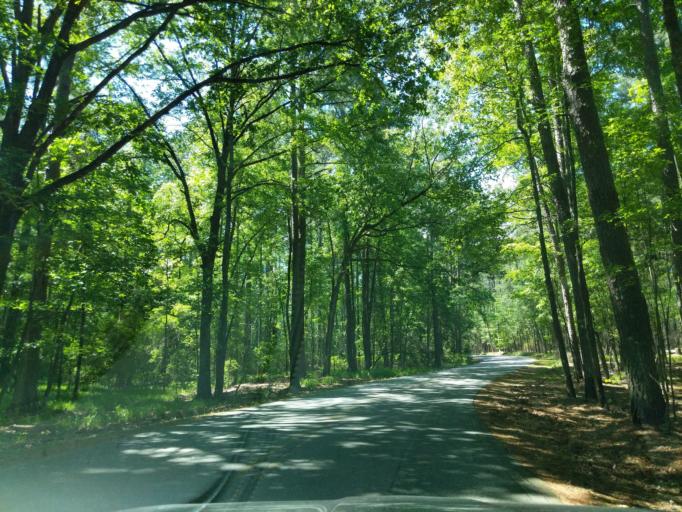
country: US
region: Georgia
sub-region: Columbia County
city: Appling
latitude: 33.6632
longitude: -82.3830
